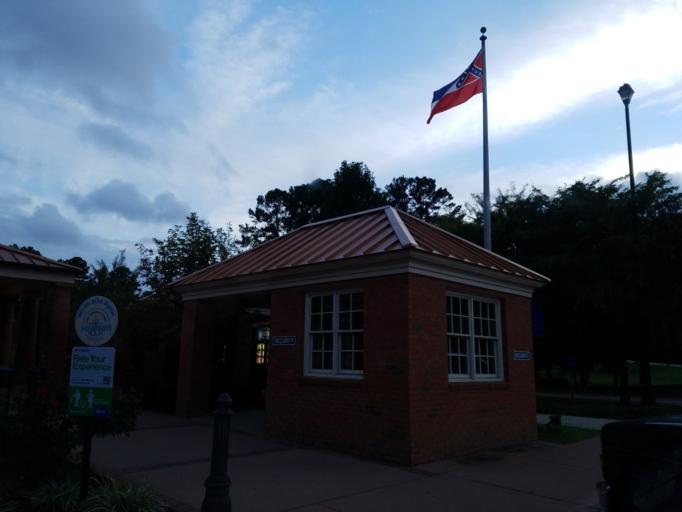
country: US
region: Mississippi
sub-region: Lauderdale County
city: Marion
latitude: 32.4110
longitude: -88.5346
